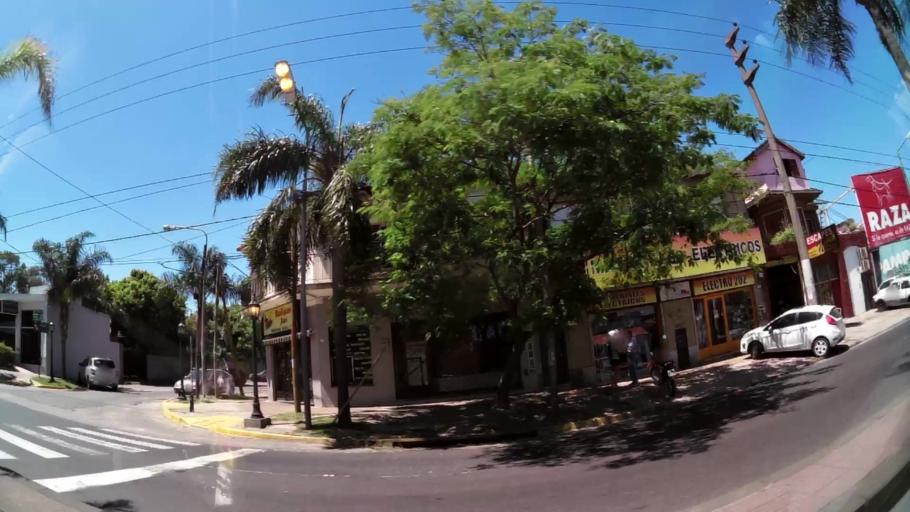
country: AR
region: Buenos Aires
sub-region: Partido de Tigre
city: Tigre
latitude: -34.4961
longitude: -58.6351
